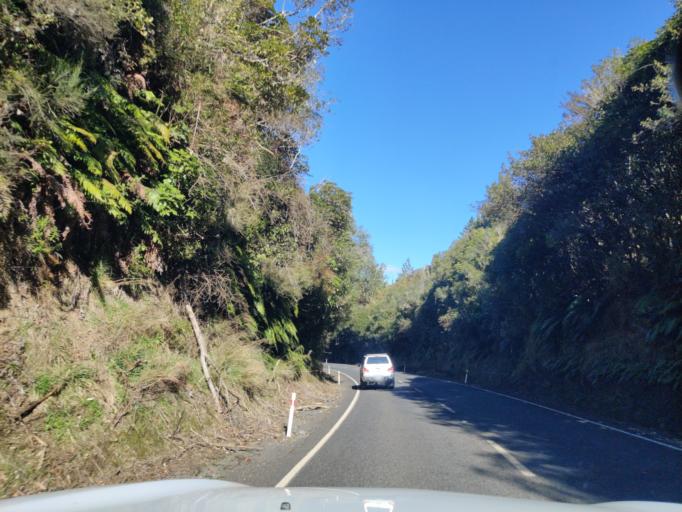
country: NZ
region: Waikato
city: Turangi
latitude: -38.7528
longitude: 175.6756
